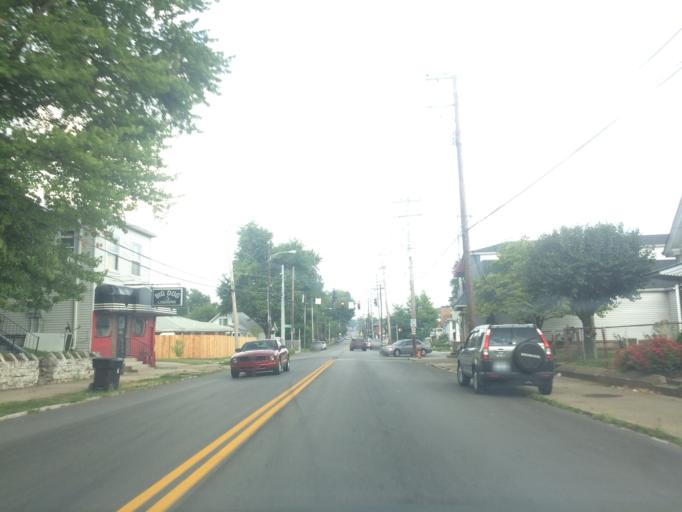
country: US
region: Kentucky
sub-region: Jefferson County
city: Audubon Park
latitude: 38.2202
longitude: -85.7484
